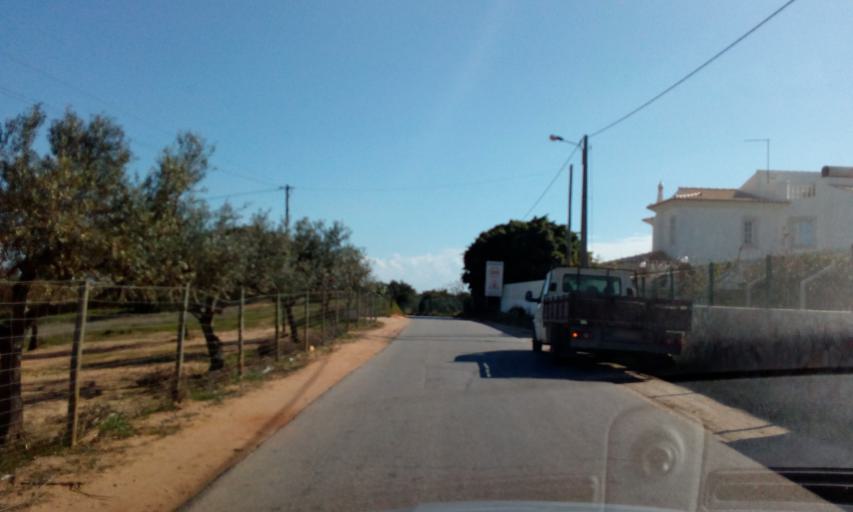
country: PT
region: Faro
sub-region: Albufeira
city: Ferreiras
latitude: 37.1004
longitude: -8.2056
